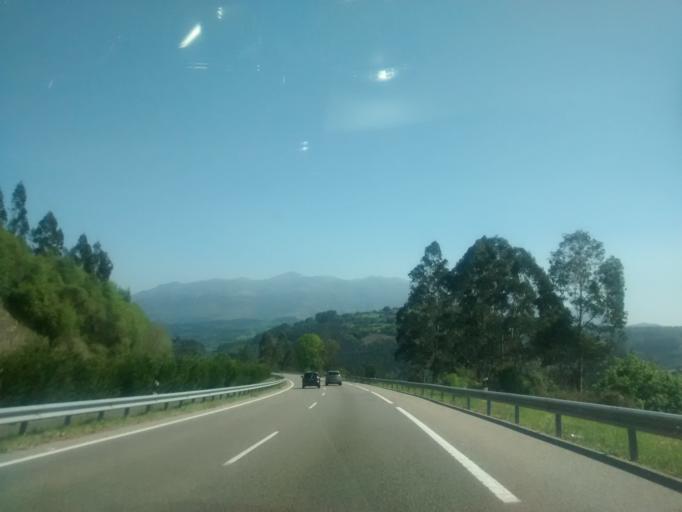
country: ES
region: Asturias
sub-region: Province of Asturias
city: Colunga
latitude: 43.4960
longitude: -5.3280
